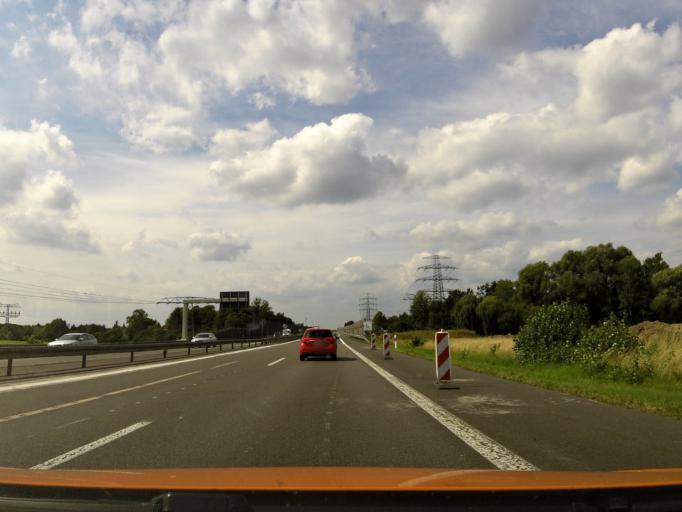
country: DE
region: Berlin
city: Buch
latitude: 52.6192
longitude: 13.5077
